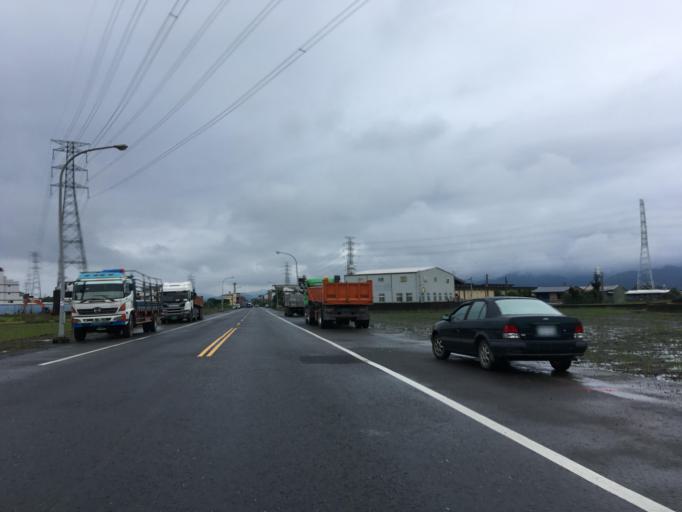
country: TW
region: Taiwan
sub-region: Yilan
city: Yilan
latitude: 24.6634
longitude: 121.7512
